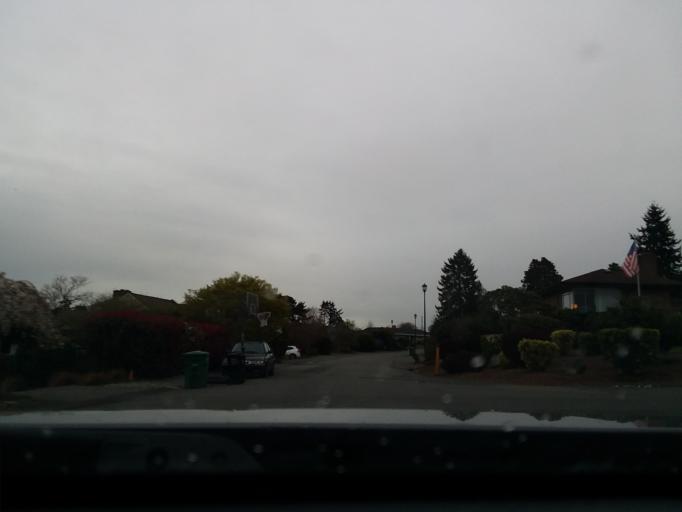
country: US
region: Washington
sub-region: King County
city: Shoreline
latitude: 47.7072
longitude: -122.3728
